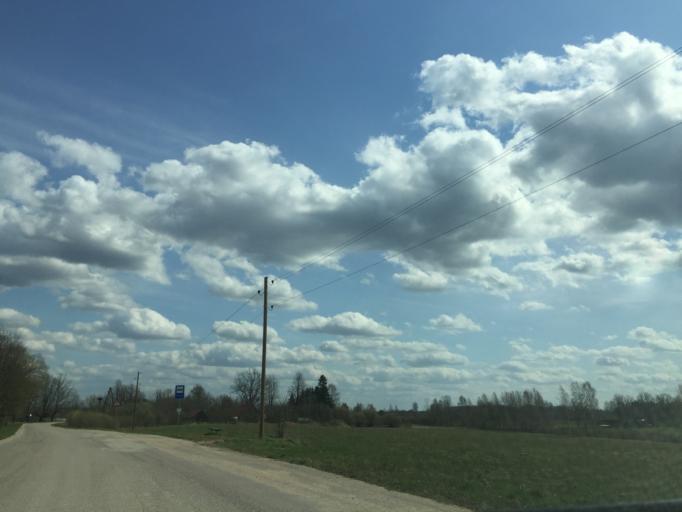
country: LV
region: Skriveri
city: Skriveri
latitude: 56.7449
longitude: 25.1006
